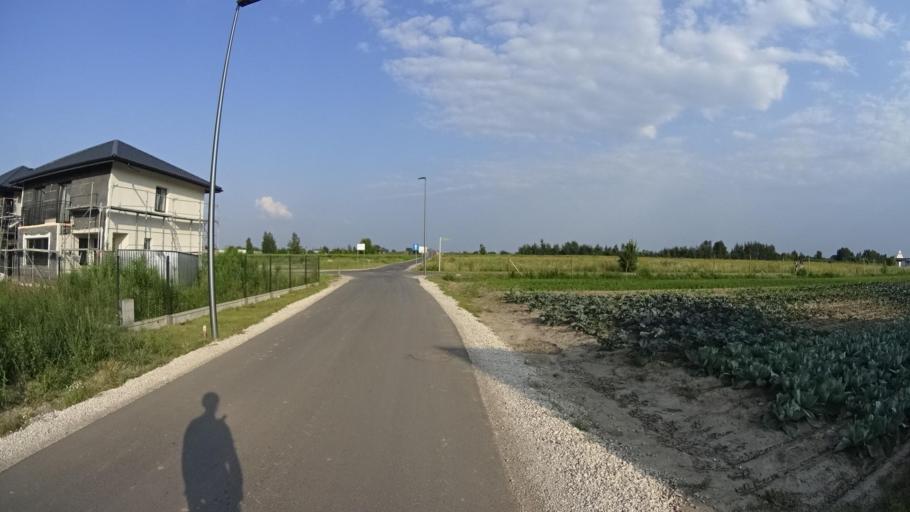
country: PL
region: Masovian Voivodeship
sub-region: Powiat pruszkowski
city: Nowe Grocholice
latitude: 52.1668
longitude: 20.9013
